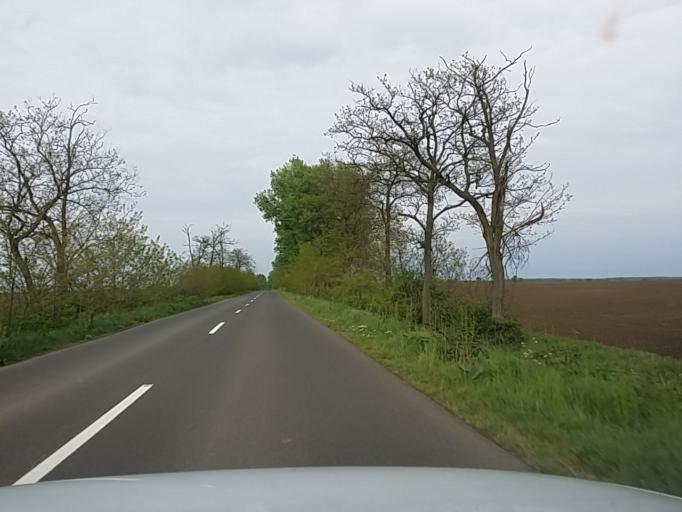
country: HU
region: Pest
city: Zsambok
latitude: 47.5500
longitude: 19.6305
